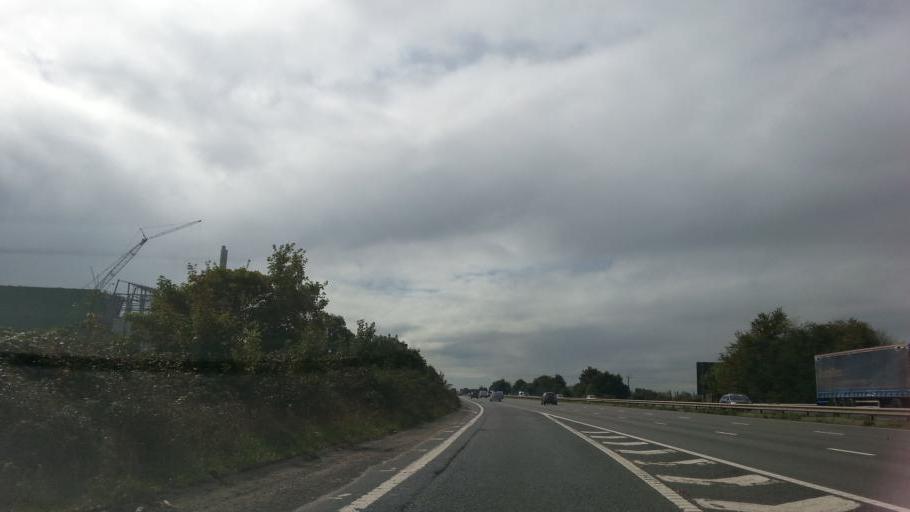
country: GB
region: England
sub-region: Gloucestershire
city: Stonehouse
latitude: 51.7959
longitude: -2.2916
